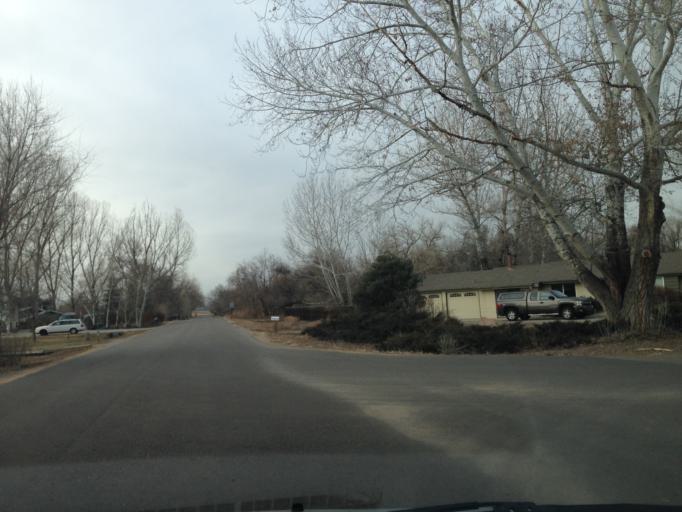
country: US
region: Colorado
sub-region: Boulder County
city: Erie
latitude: 40.0447
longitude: -105.0918
